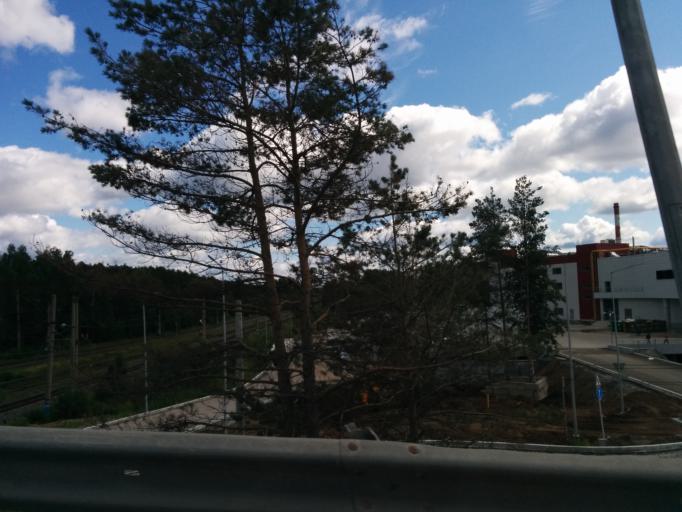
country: RU
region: Perm
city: Perm
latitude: 58.0401
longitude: 56.1879
